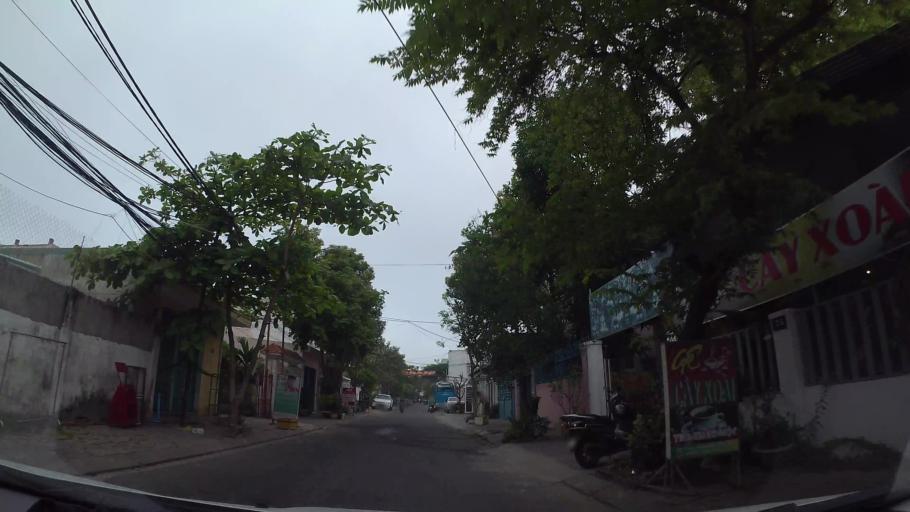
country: VN
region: Da Nang
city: Son Tra
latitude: 16.0404
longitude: 108.2455
